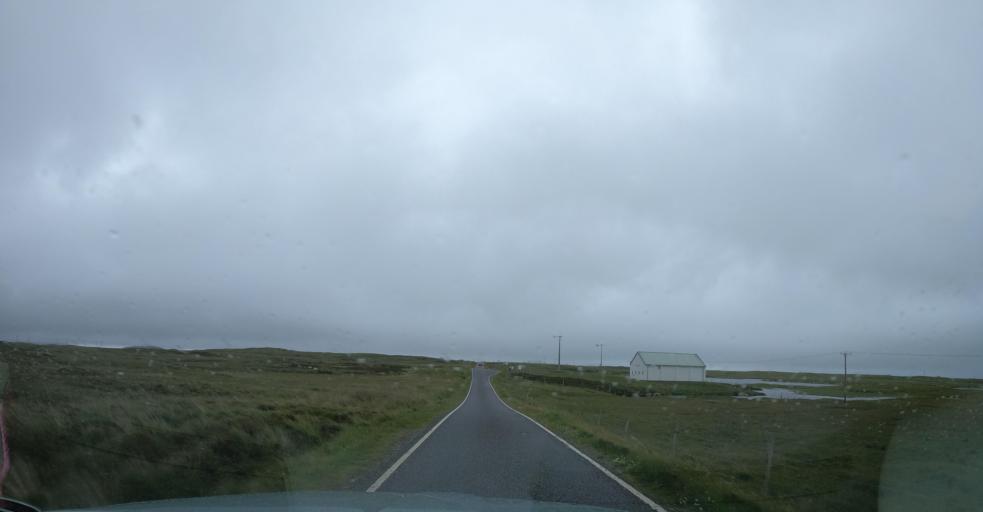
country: GB
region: Scotland
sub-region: Eilean Siar
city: Isle of North Uist
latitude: 57.5466
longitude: -7.3270
